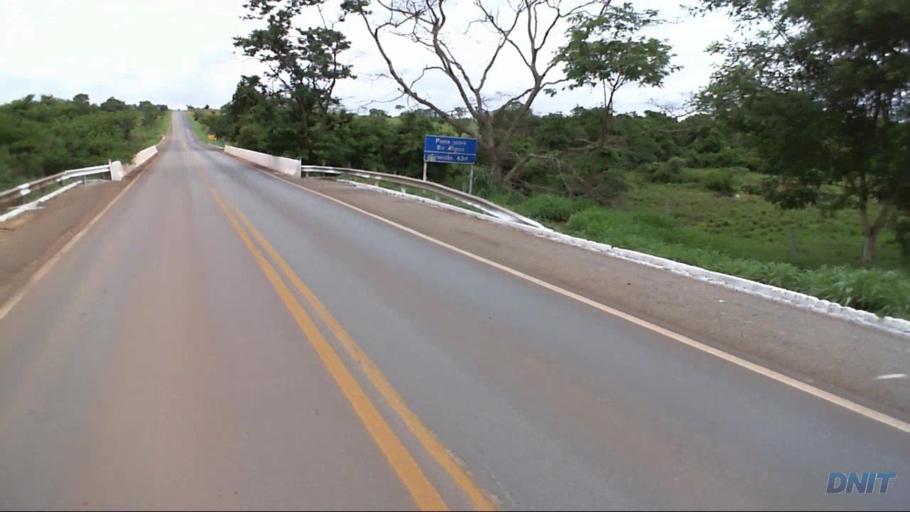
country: BR
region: Goias
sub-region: Padre Bernardo
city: Padre Bernardo
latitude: -15.1575
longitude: -48.3194
